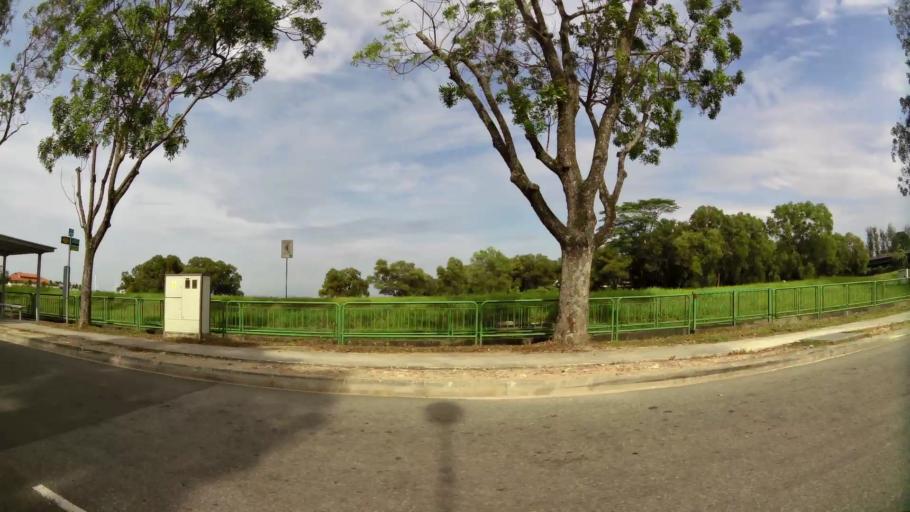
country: MY
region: Johor
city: Johor Bahru
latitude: 1.3445
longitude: 103.6384
